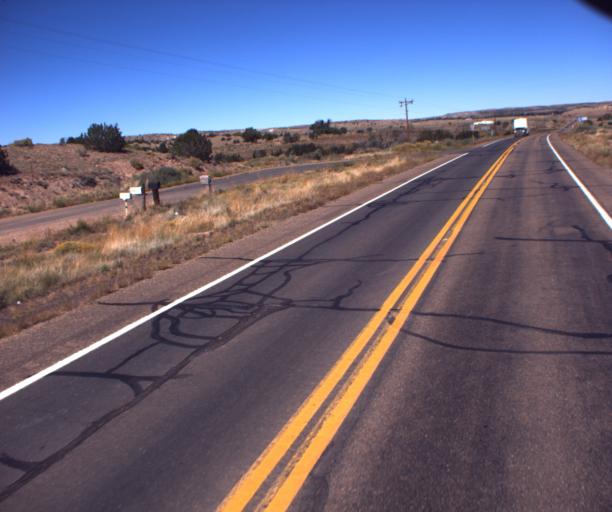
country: US
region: Arizona
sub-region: Apache County
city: Saint Johns
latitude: 34.4035
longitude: -109.4107
